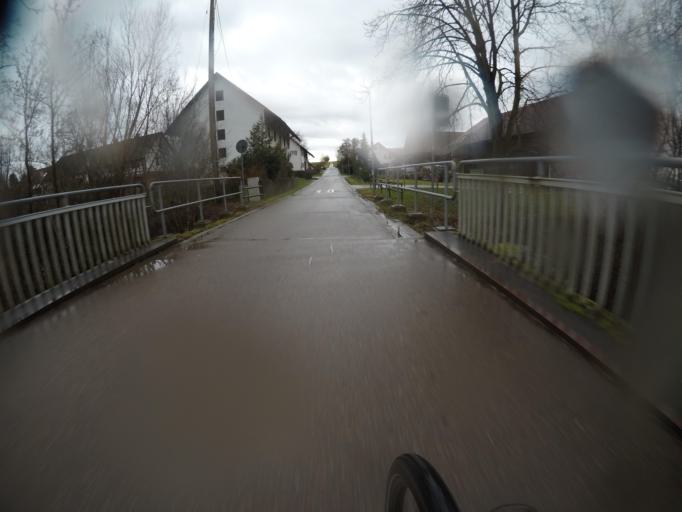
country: DE
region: Baden-Wuerttemberg
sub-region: Regierungsbezirk Stuttgart
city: Asperg
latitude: 48.9348
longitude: 9.1584
